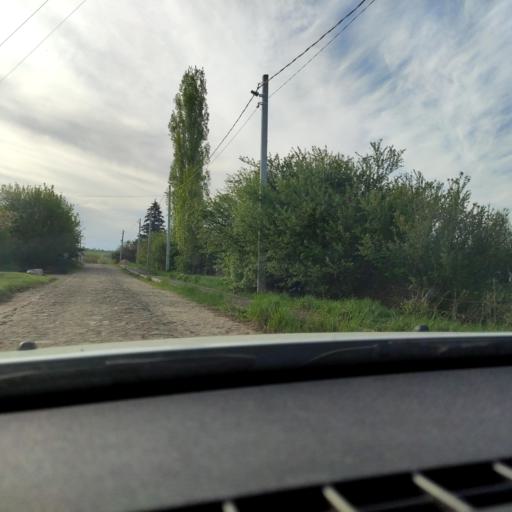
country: RU
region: Voronezj
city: Devitsa
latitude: 51.6413
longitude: 38.9556
